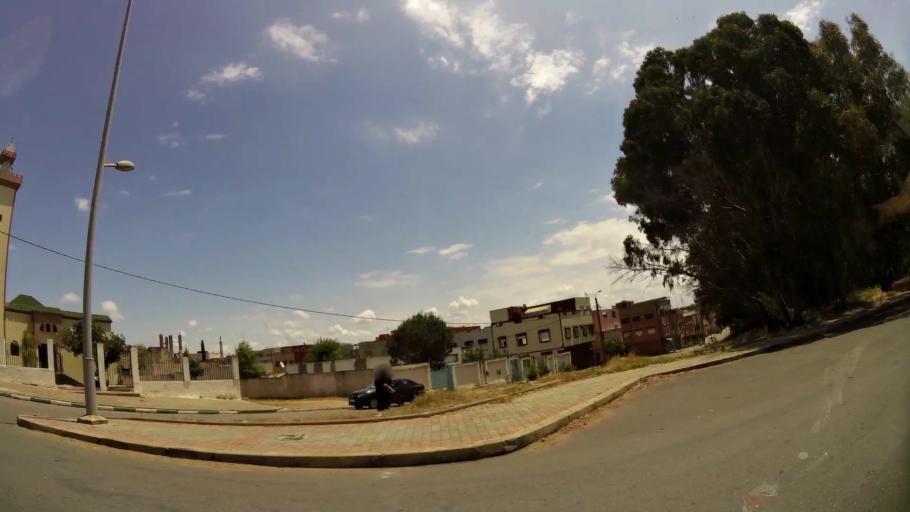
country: MA
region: Gharb-Chrarda-Beni Hssen
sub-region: Kenitra Province
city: Kenitra
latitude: 34.2635
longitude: -6.6130
